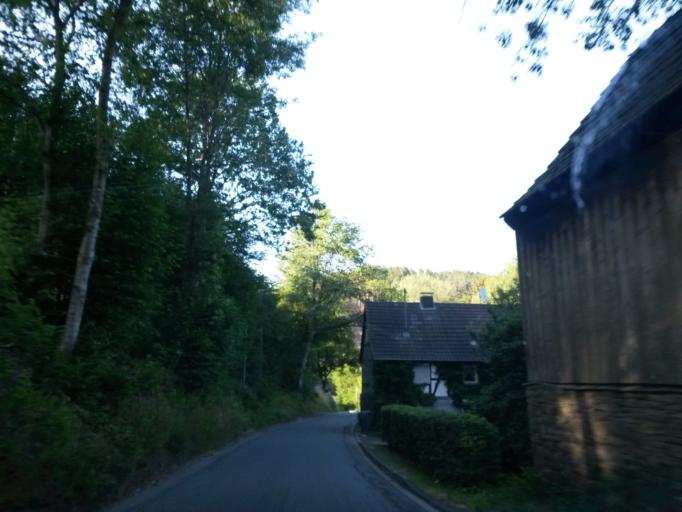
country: DE
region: North Rhine-Westphalia
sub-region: Regierungsbezirk Koln
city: Marienheide
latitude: 51.0475
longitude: 7.5036
